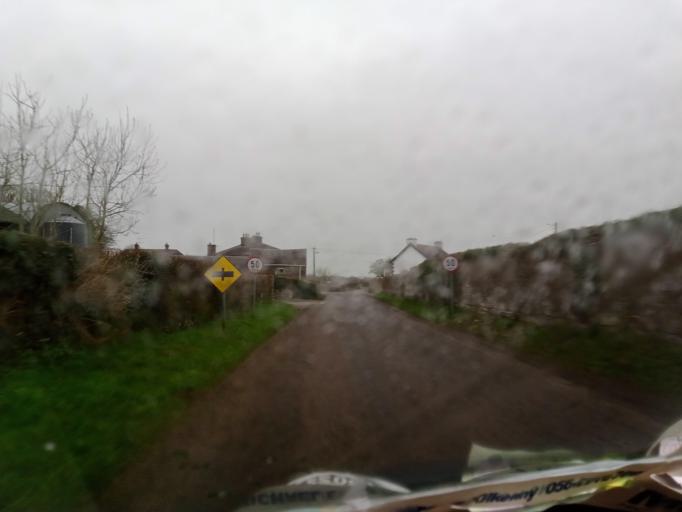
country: IE
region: Munster
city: Fethard
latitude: 52.5630
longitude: -7.7672
